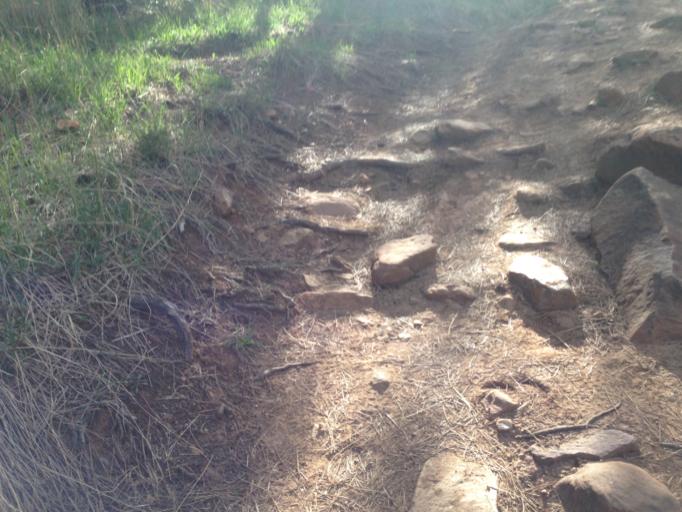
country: US
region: Colorado
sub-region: Boulder County
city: Boulder
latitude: 39.9460
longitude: -105.2786
